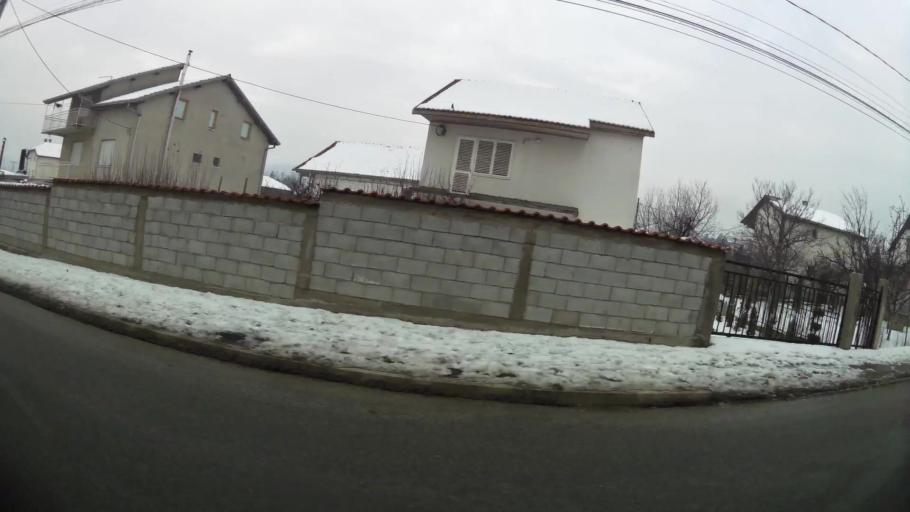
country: MK
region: Saraj
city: Saraj
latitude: 42.0321
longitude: 21.3439
